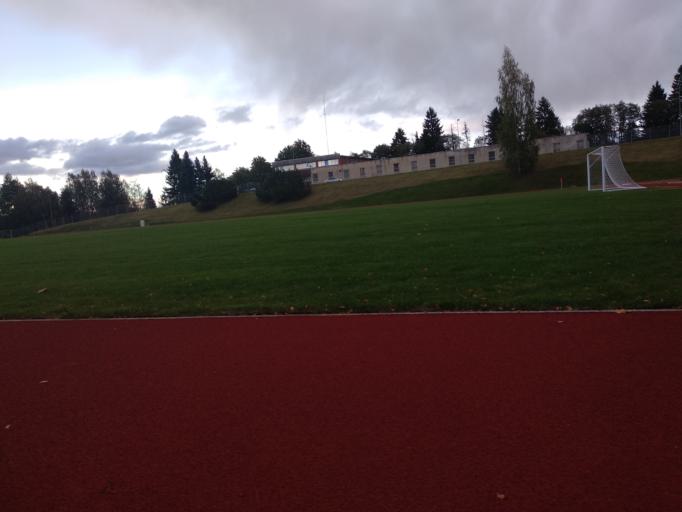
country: EE
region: Polvamaa
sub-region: Polva linn
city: Polva
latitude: 58.0497
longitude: 27.0529
